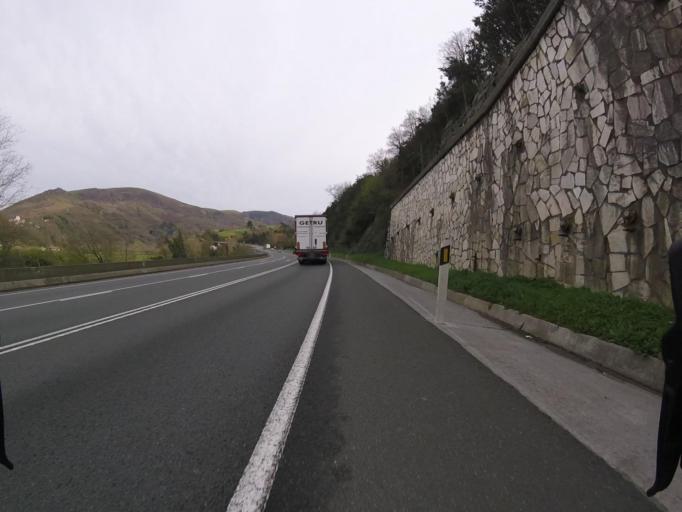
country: ES
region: Basque Country
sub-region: Provincia de Guipuzcoa
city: Irun
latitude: 43.3328
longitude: -1.7529
